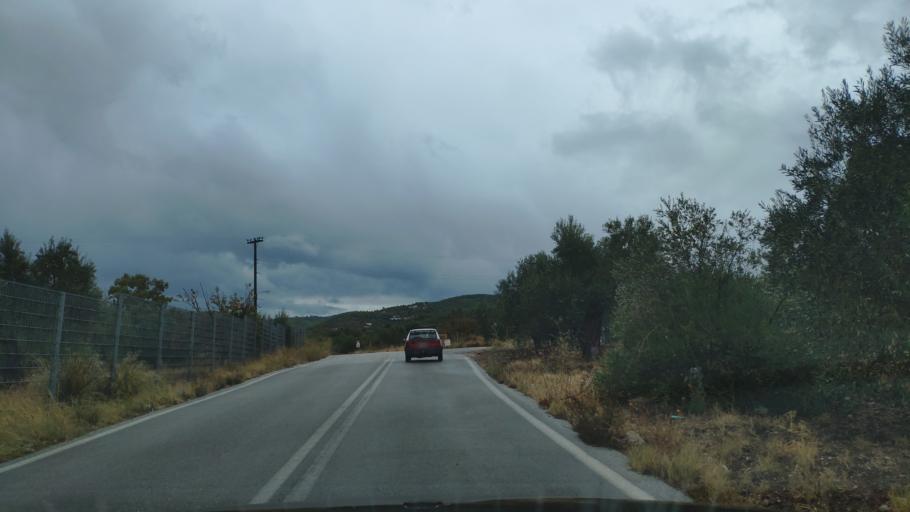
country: GR
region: Peloponnese
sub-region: Nomos Korinthias
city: Perachora
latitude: 38.0137
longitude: 22.9460
